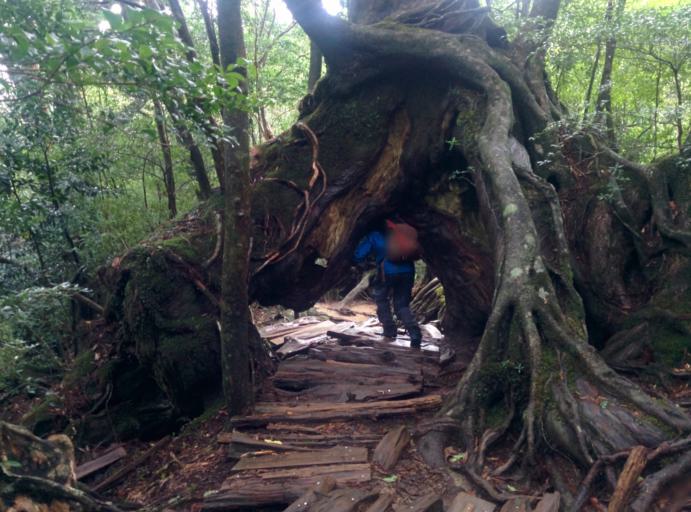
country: JP
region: Kagoshima
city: Nishinoomote
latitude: 30.3700
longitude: 130.5708
